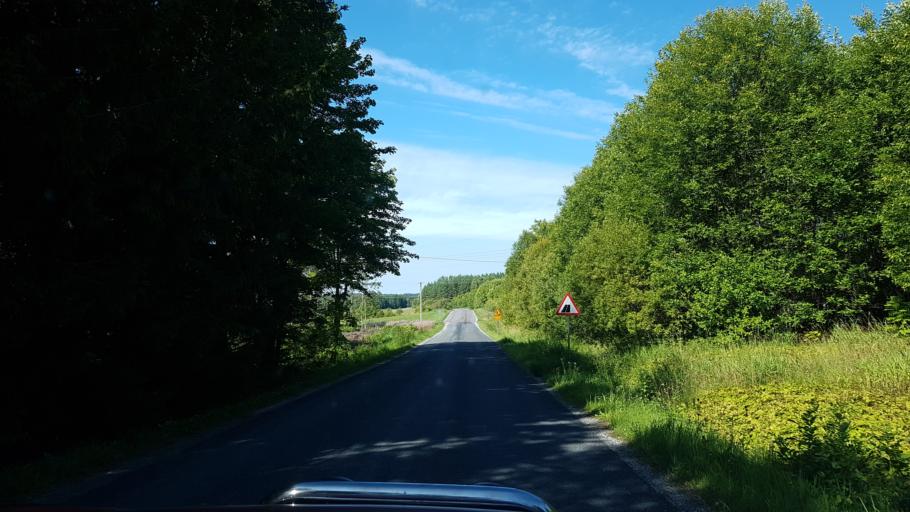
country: EE
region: Tartu
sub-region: Elva linn
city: Elva
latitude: 58.2433
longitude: 26.3985
